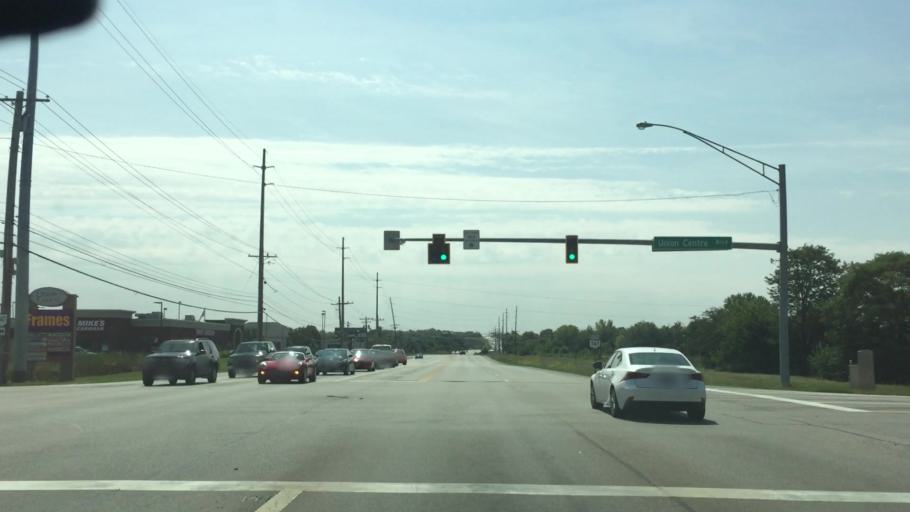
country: US
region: Ohio
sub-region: Butler County
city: Beckett Ridge
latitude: 39.3428
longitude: -84.4617
